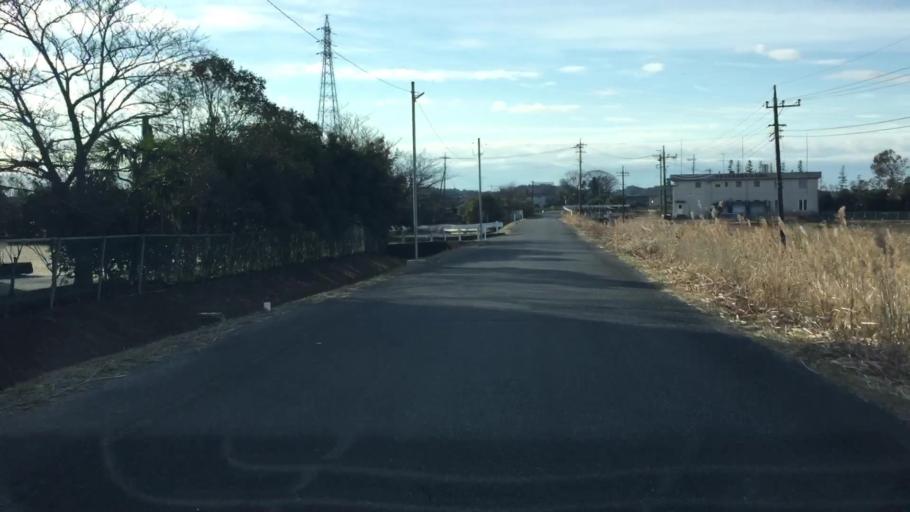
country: JP
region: Ibaraki
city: Toride
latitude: 35.8444
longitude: 140.1290
